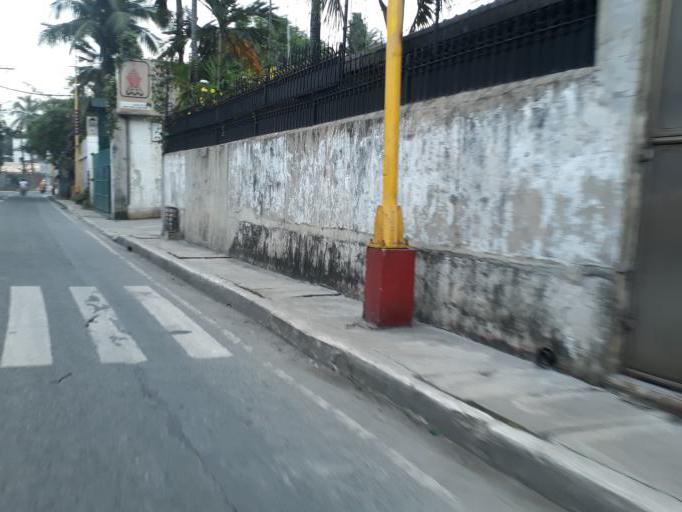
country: PH
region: Calabarzon
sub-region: Province of Rizal
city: Navotas
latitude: 14.6636
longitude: 120.9450
